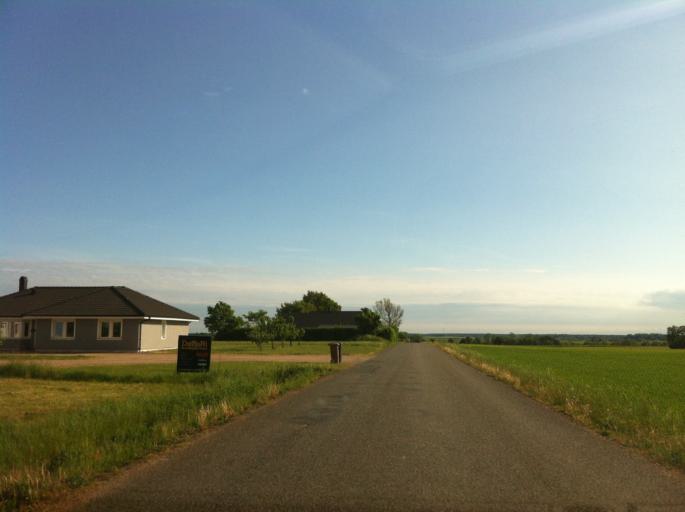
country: SE
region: Skane
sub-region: Svalovs Kommun
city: Kagerod
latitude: 55.9912
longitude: 13.0766
